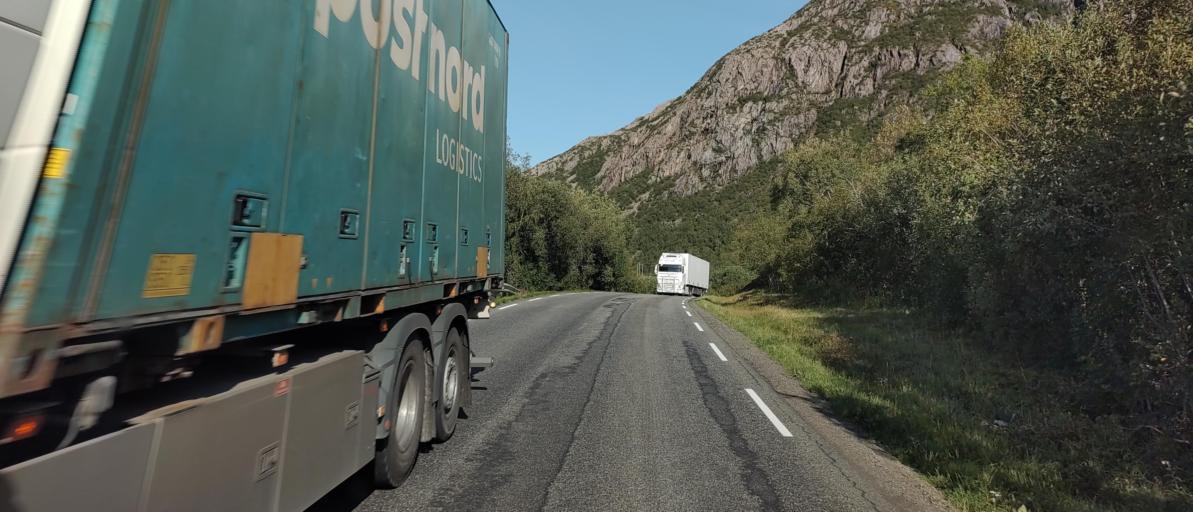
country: NO
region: Nordland
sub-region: Vagan
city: Svolvaer
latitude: 68.2794
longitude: 14.6608
